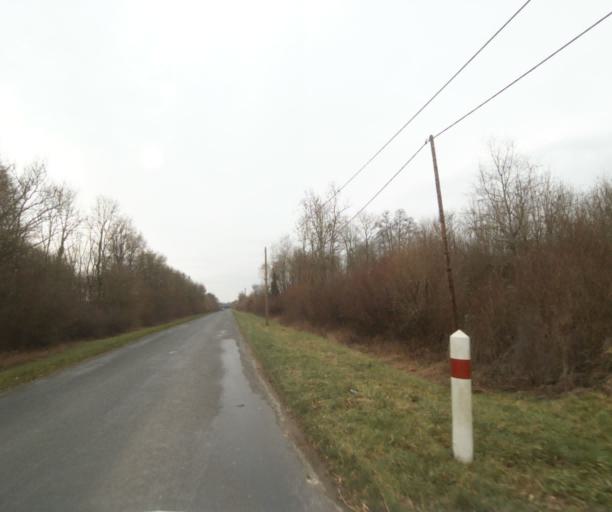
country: FR
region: Champagne-Ardenne
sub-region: Departement de la Haute-Marne
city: Villiers-en-Lieu
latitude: 48.6541
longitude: 4.8765
